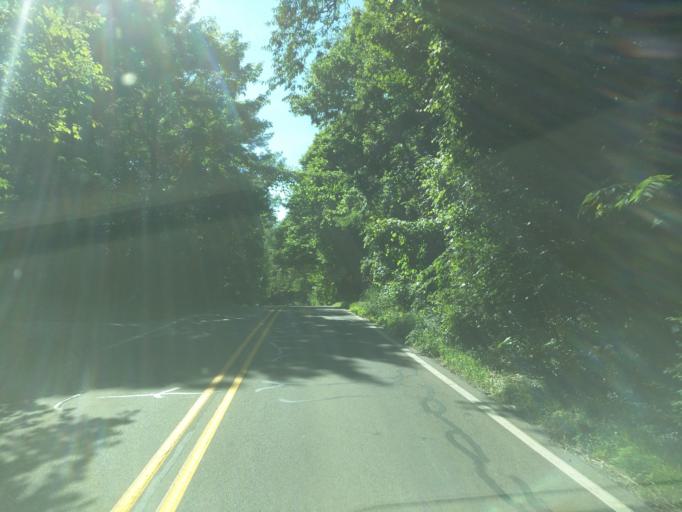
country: US
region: Michigan
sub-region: Eaton County
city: Waverly
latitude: 42.7637
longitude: -84.6133
